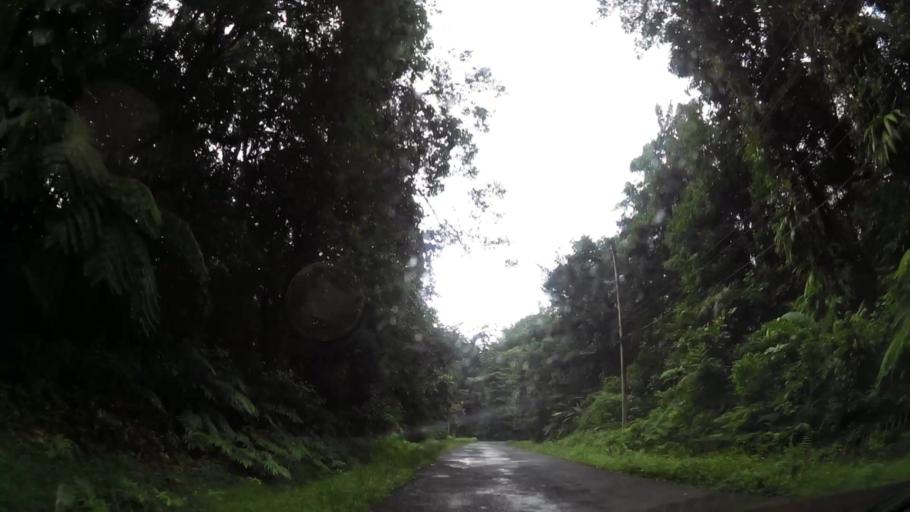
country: DM
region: Saint Paul
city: Pont Casse
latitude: 15.3912
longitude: -61.3109
